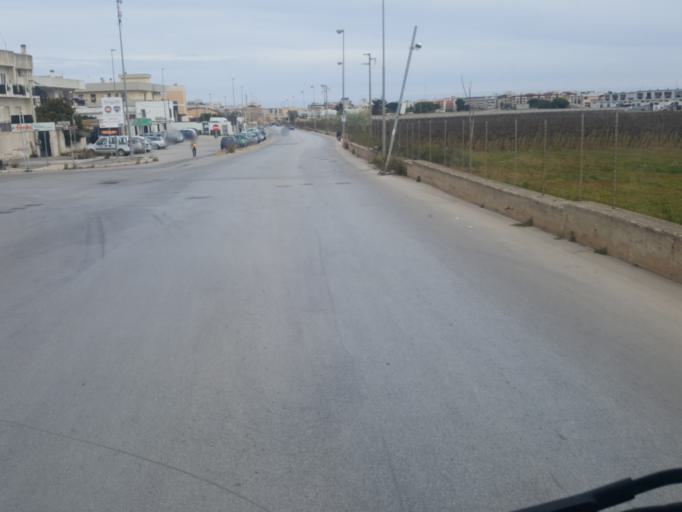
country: IT
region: Apulia
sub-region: Provincia di Barletta - Andria - Trani
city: Bisceglie
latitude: 41.2265
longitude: 16.5049
